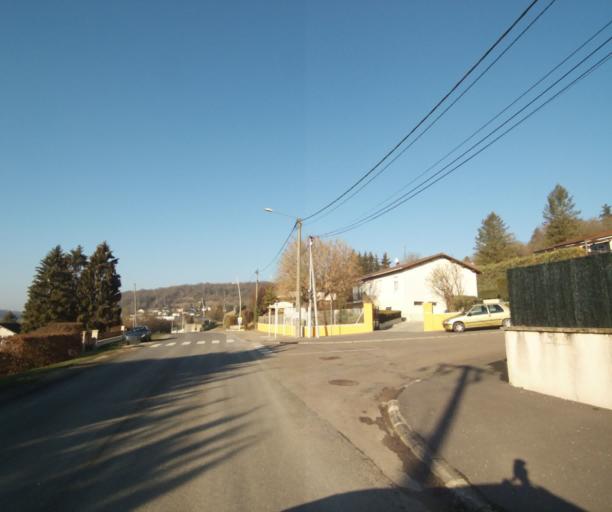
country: FR
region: Champagne-Ardenne
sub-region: Departement de la Haute-Marne
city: Chevillon
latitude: 48.5205
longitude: 5.1175
